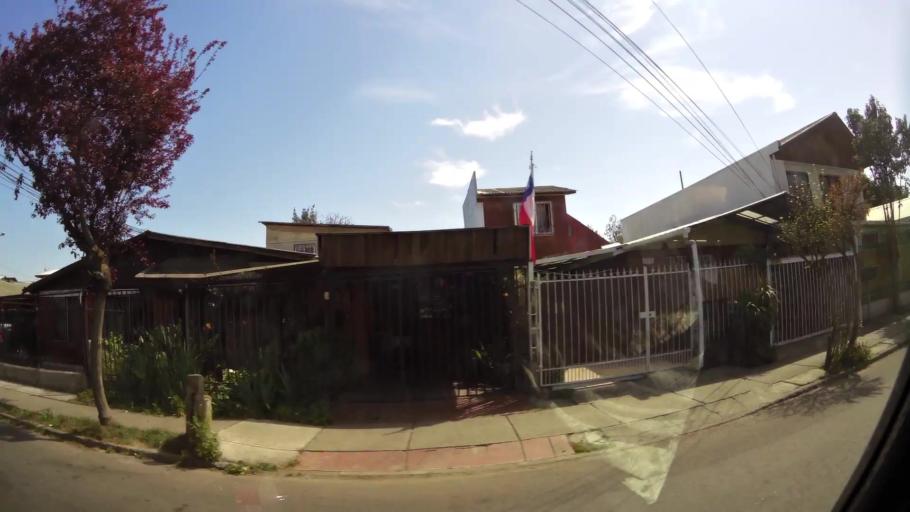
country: CL
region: Santiago Metropolitan
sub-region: Provincia de Santiago
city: Lo Prado
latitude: -33.4731
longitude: -70.7249
